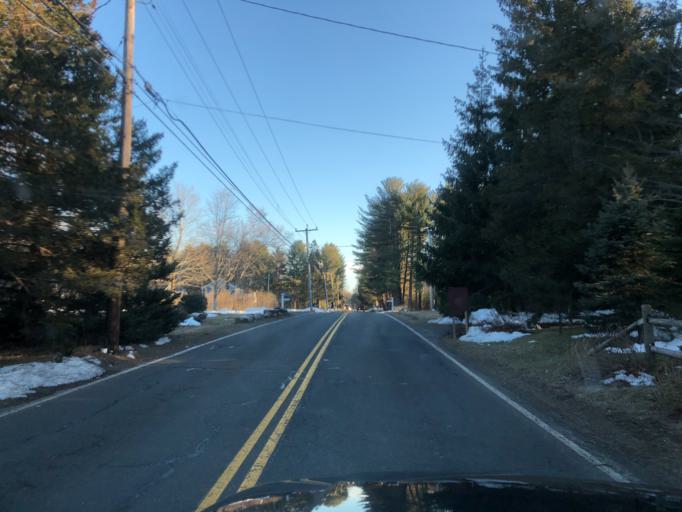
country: US
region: Connecticut
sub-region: Hartford County
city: Farmington
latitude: 41.7646
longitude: -72.8584
